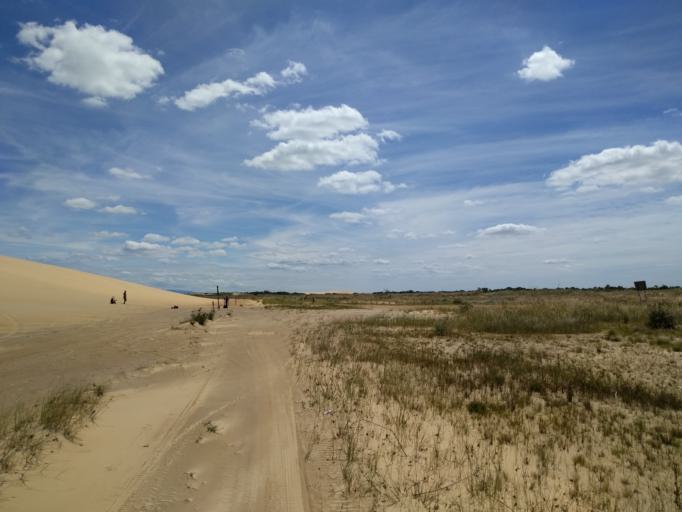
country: BO
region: Santa Cruz
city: Santa Cruz de la Sierra
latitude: -17.9400
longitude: -63.1577
